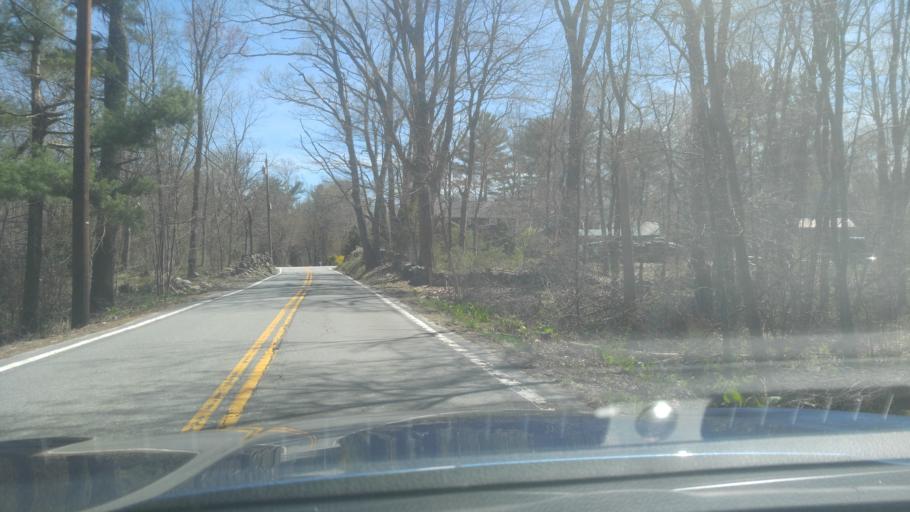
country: US
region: Rhode Island
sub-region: Washington County
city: Hope Valley
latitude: 41.5775
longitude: -71.7553
